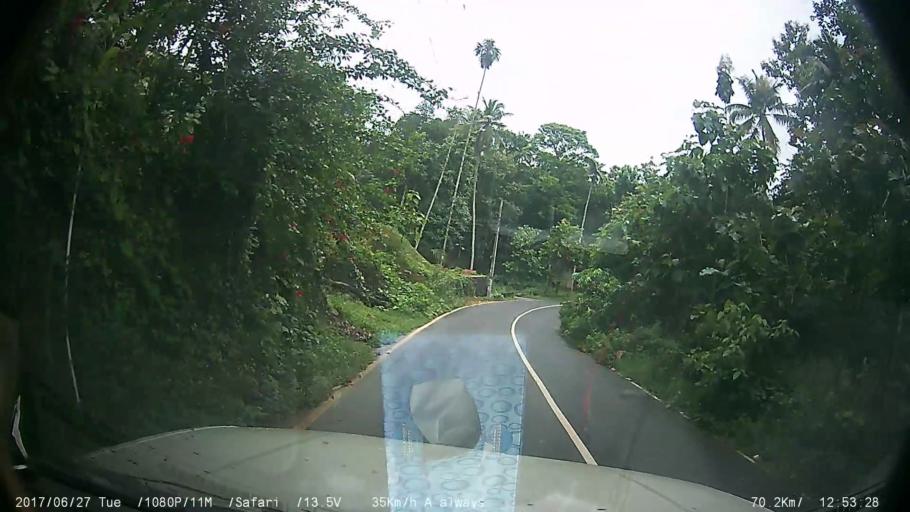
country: IN
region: Kerala
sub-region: Kottayam
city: Palackattumala
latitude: 9.7801
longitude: 76.5437
